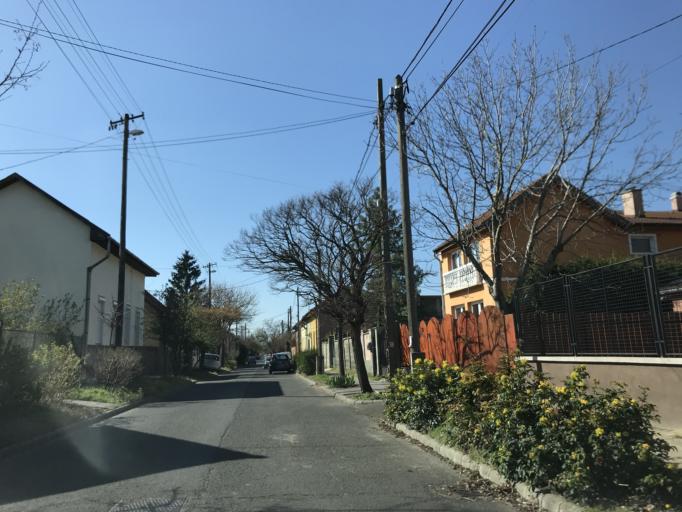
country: HU
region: Budapest
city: Budapest XV. keruelet
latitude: 47.5582
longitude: 19.1171
